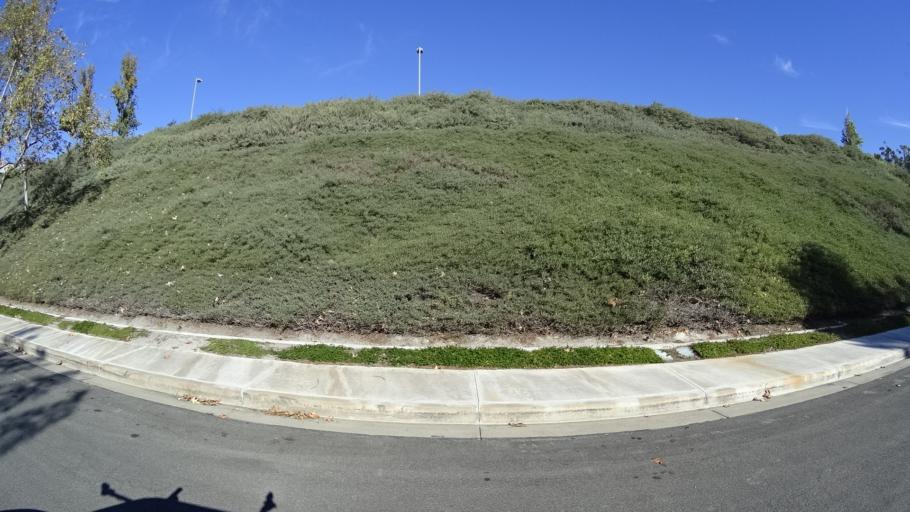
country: US
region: California
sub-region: Orange County
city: Foothill Ranch
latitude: 33.6772
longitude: -117.6575
